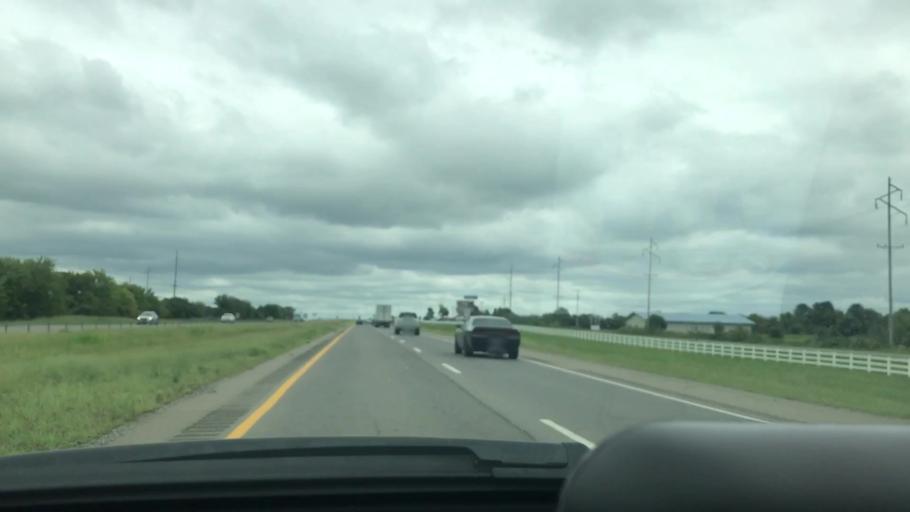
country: US
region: Oklahoma
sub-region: McIntosh County
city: Checotah
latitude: 35.4654
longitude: -95.5407
